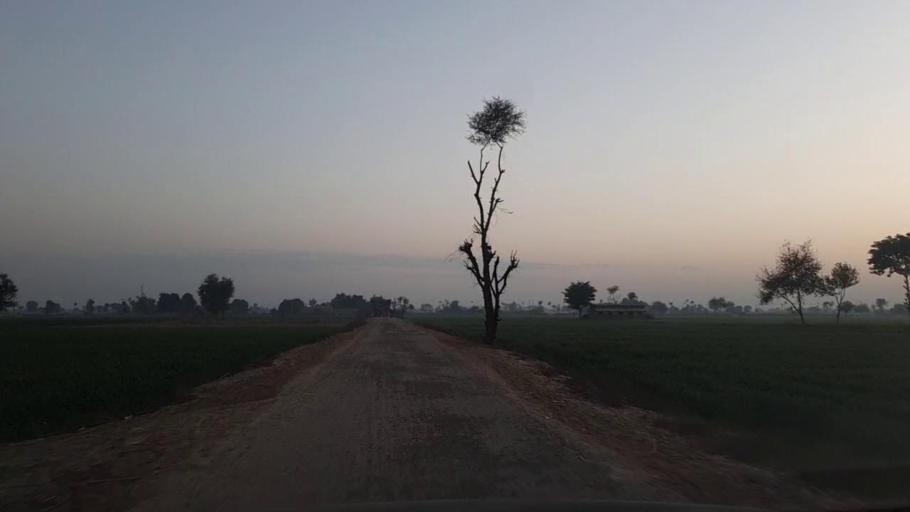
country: PK
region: Sindh
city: Daur
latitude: 26.4788
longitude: 68.4875
